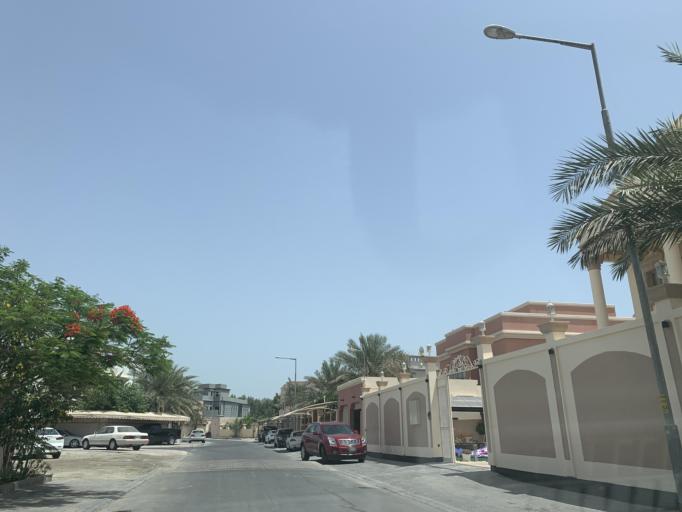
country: BH
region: Northern
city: Madinat `Isa
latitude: 26.1625
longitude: 50.5777
